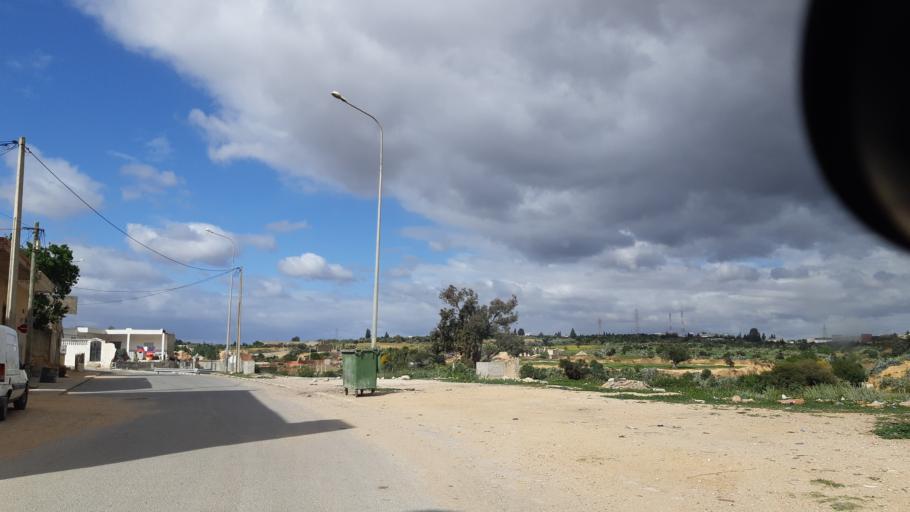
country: TN
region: Susah
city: Akouda
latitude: 35.8733
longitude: 10.5189
